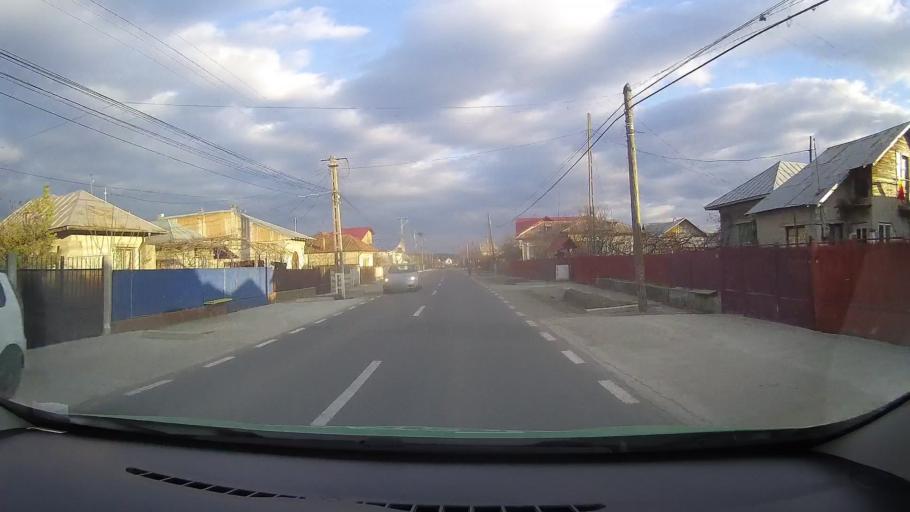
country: RO
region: Dambovita
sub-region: Comuna I. L. Caragiale
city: Ghirdoveni
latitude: 44.9424
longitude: 25.6684
